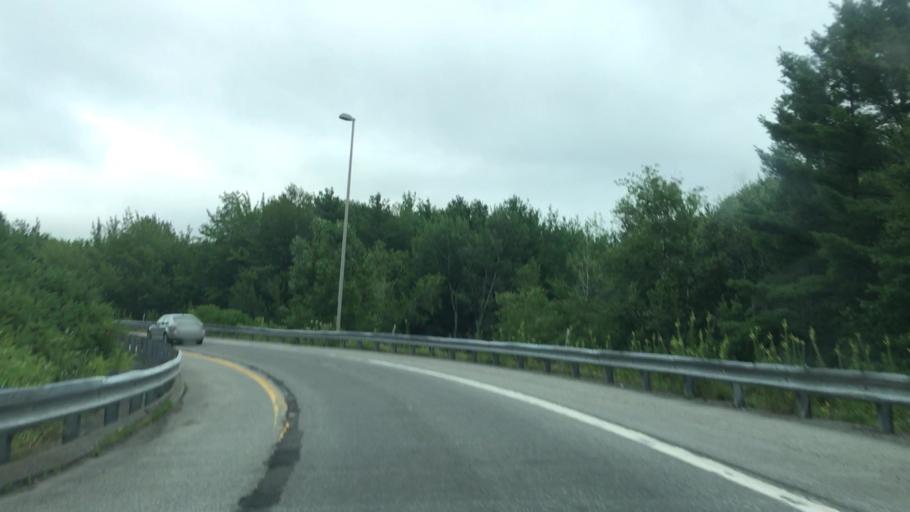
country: US
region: Maine
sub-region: Penobscot County
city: Brewer
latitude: 44.8235
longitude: -68.7553
